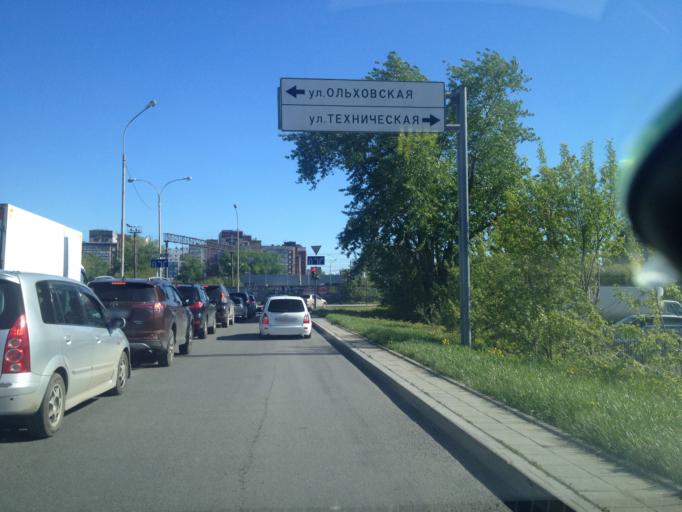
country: RU
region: Sverdlovsk
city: Yekaterinburg
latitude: 56.8595
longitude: 60.5518
